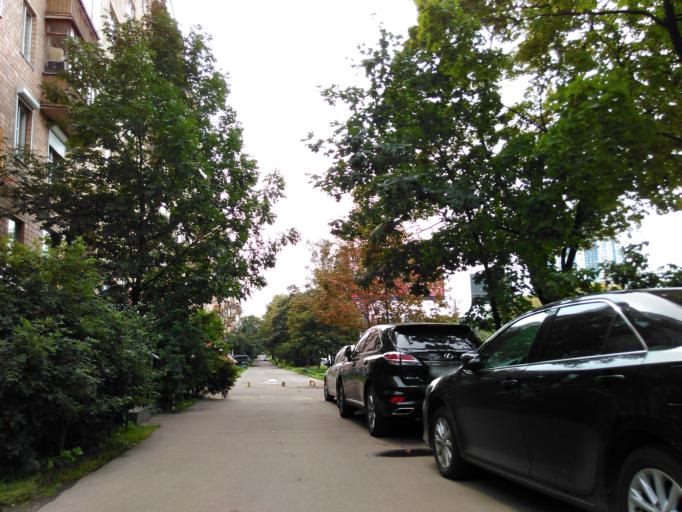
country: RU
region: Moscow
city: Vorob'yovo
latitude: 55.7163
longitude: 37.5172
